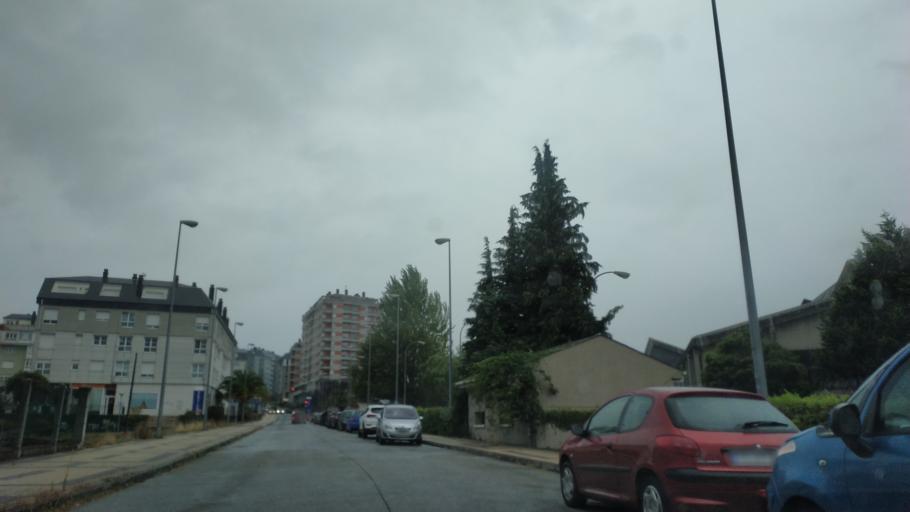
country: ES
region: Galicia
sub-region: Provincia de Lugo
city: Lugo
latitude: 42.9930
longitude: -7.5503
